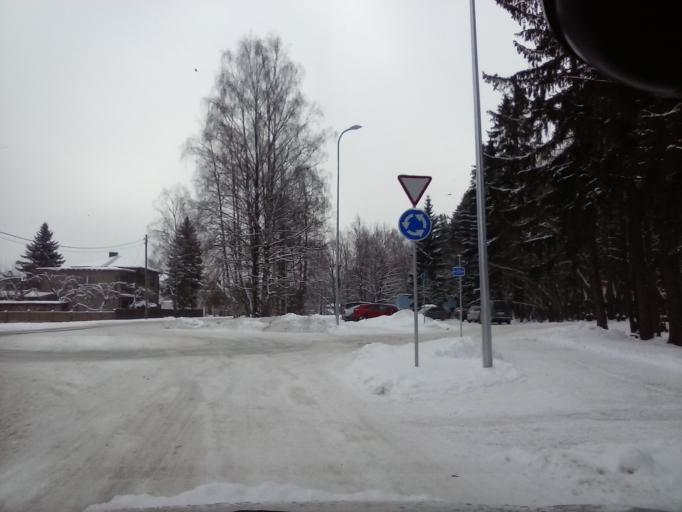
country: EE
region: Tartu
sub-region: Tartu linn
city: Tartu
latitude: 58.3637
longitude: 26.6880
